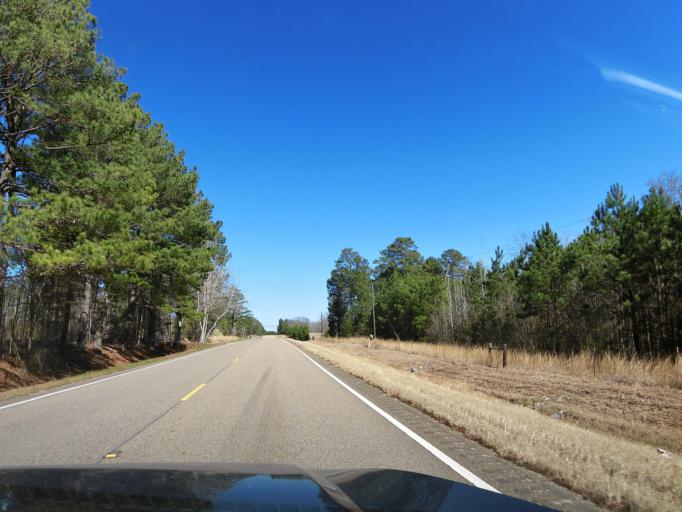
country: US
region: Alabama
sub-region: Bullock County
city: Union Springs
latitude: 32.1188
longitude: -85.7809
